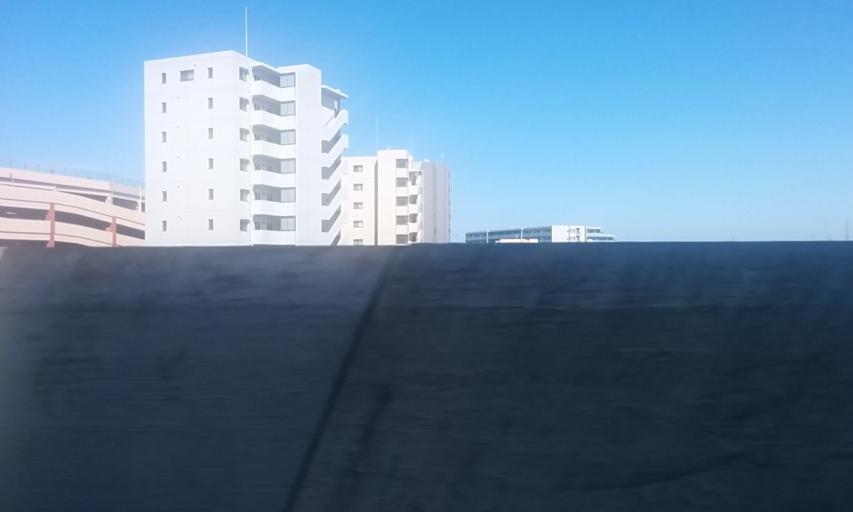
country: JP
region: Saitama
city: Yashio-shi
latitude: 35.8087
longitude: 139.8456
